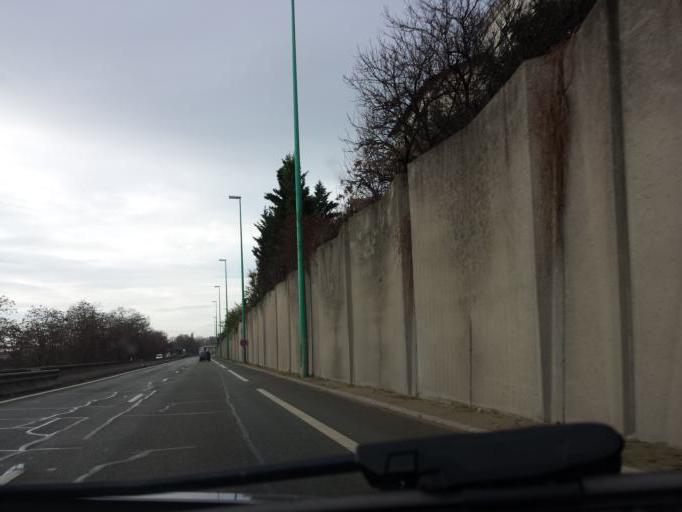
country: FR
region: Ile-de-France
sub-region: Departement du Val-d'Oise
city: Argenteuil
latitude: 48.9472
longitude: 2.2678
